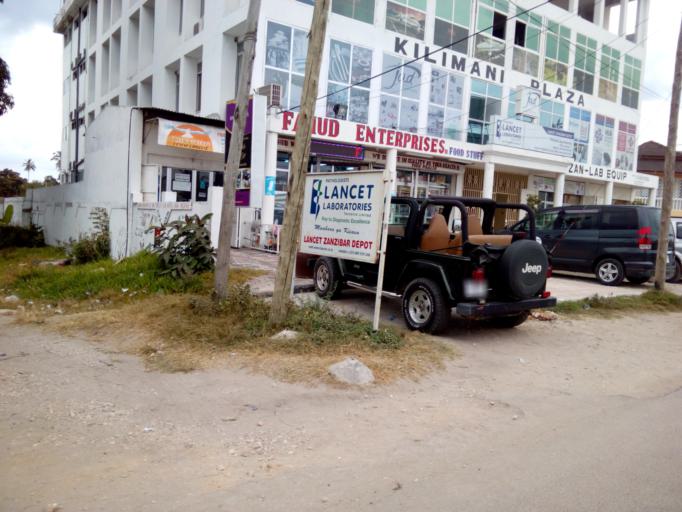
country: TZ
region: Zanzibar Urban/West
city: Zanzibar
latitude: -6.1788
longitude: 39.2041
